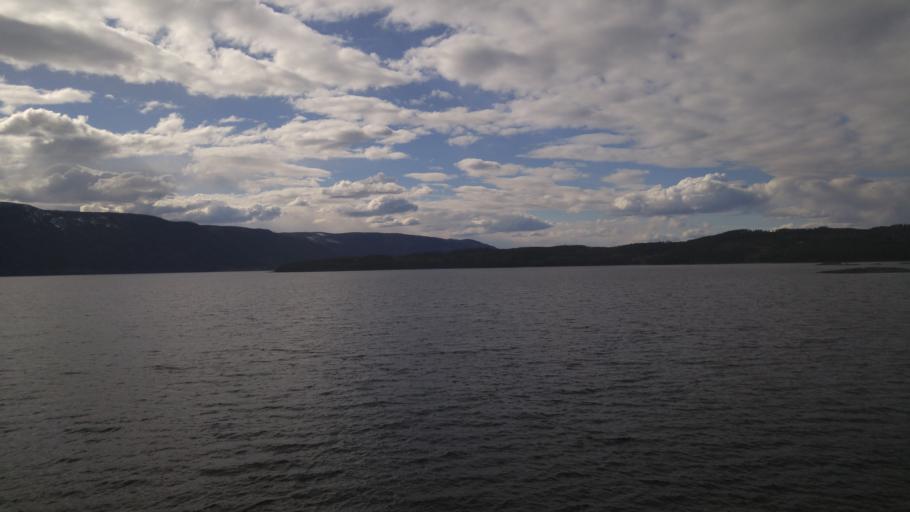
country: NO
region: Hedmark
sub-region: Stange
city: Stange
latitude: 60.5750
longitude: 11.2648
